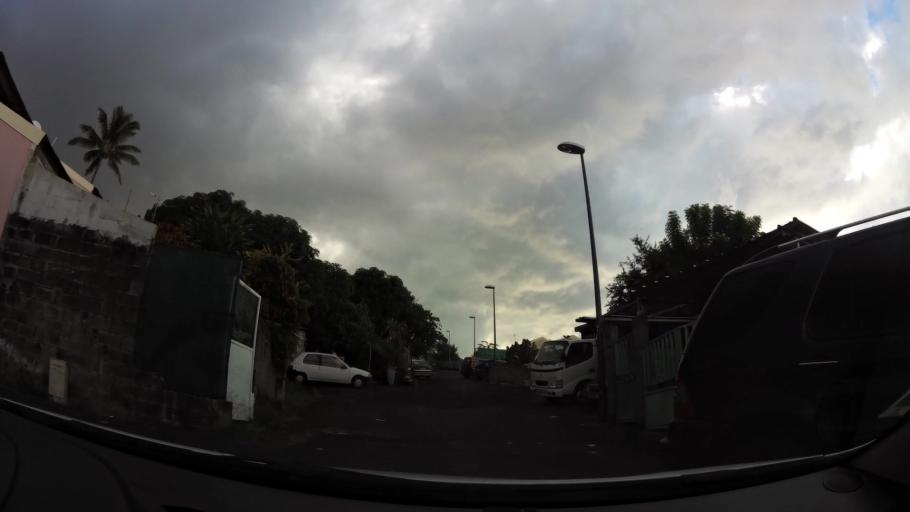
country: RE
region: Reunion
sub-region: Reunion
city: Saint-Denis
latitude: -20.9001
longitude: 55.4482
